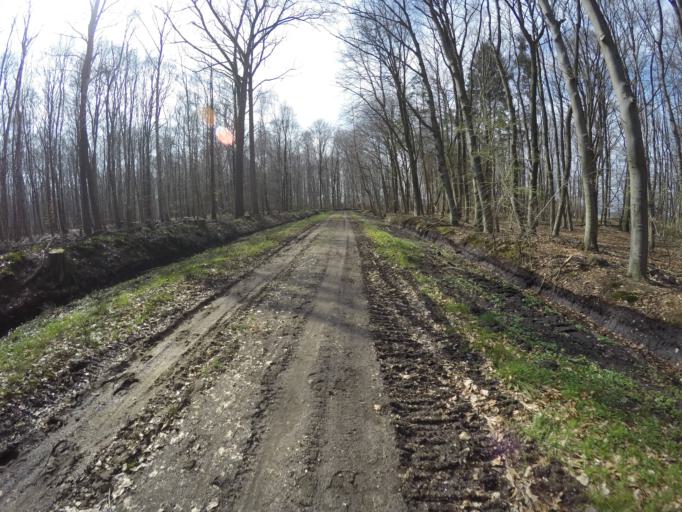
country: DE
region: Schleswig-Holstein
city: Borstel-Hohenraden
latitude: 53.7249
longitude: 9.8235
